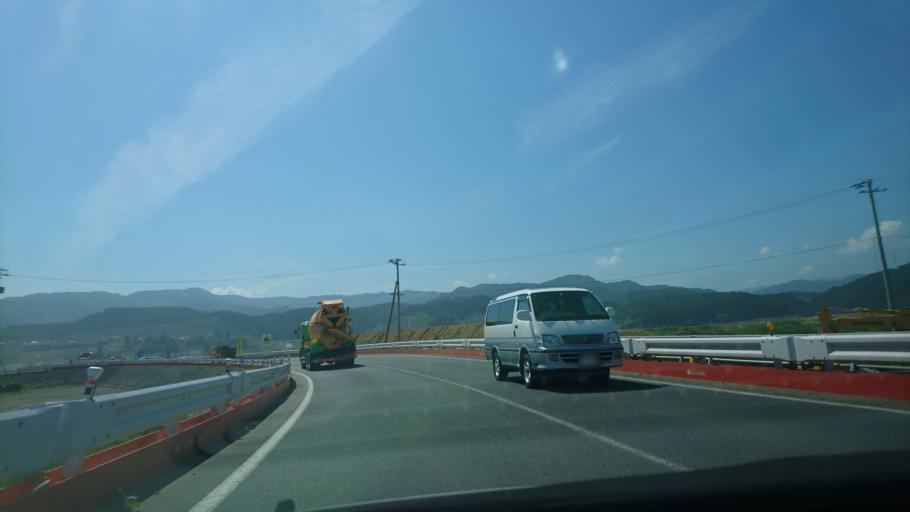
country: JP
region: Iwate
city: Ofunato
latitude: 39.0101
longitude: 141.6301
